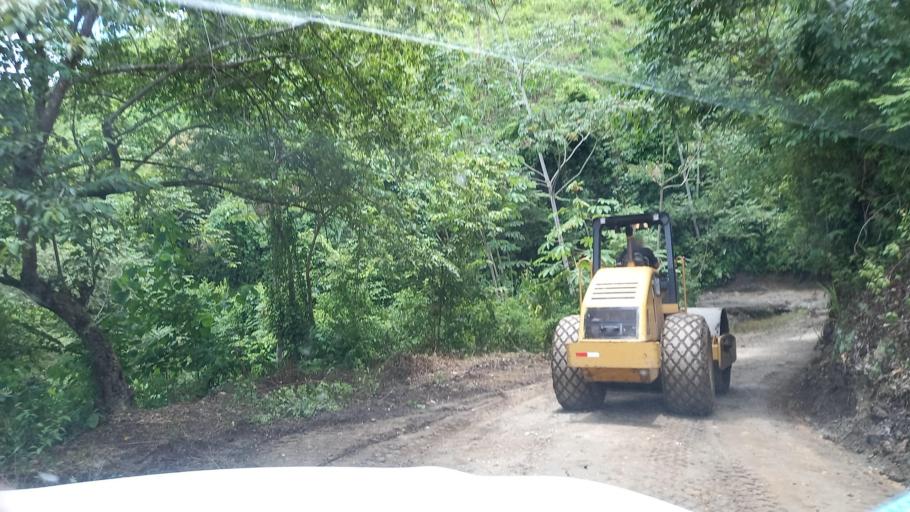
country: NI
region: Nueva Segovia
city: Wiwili
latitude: 13.7250
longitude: -85.7832
